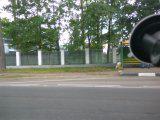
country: RU
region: Moskovskaya
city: Zhukovskiy
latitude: 55.5812
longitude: 38.1492
